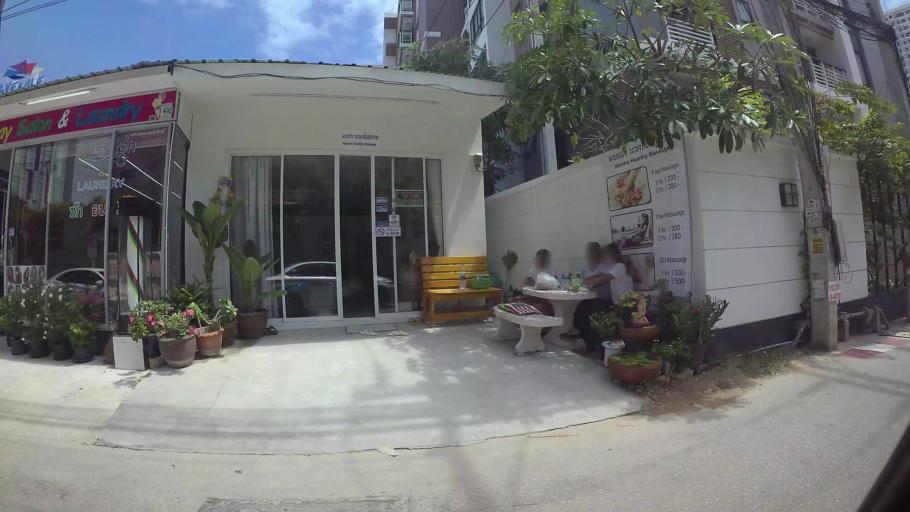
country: TH
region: Chon Buri
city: Phatthaya
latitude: 12.9290
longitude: 100.8822
